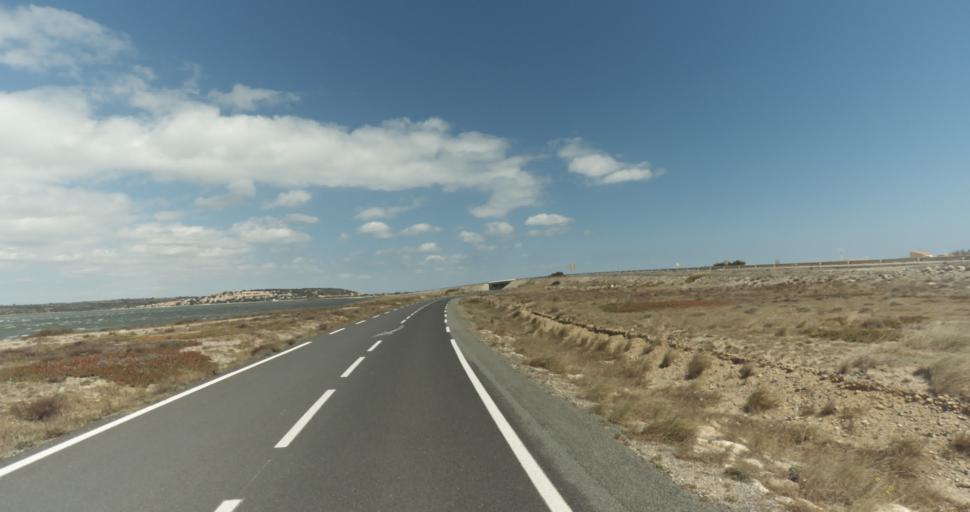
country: FR
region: Languedoc-Roussillon
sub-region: Departement de l'Aude
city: Leucate
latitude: 42.8840
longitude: 3.0454
